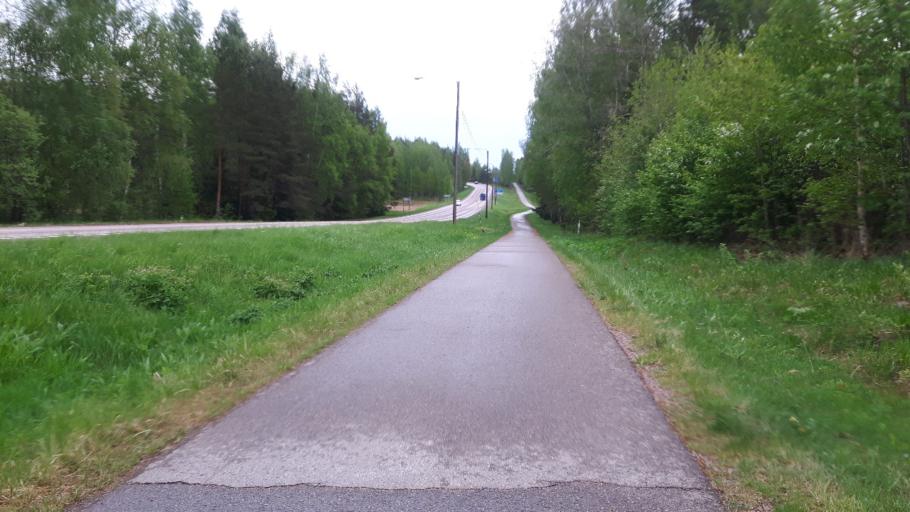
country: FI
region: Kymenlaakso
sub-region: Kotka-Hamina
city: Hamina
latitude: 60.5655
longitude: 27.1080
